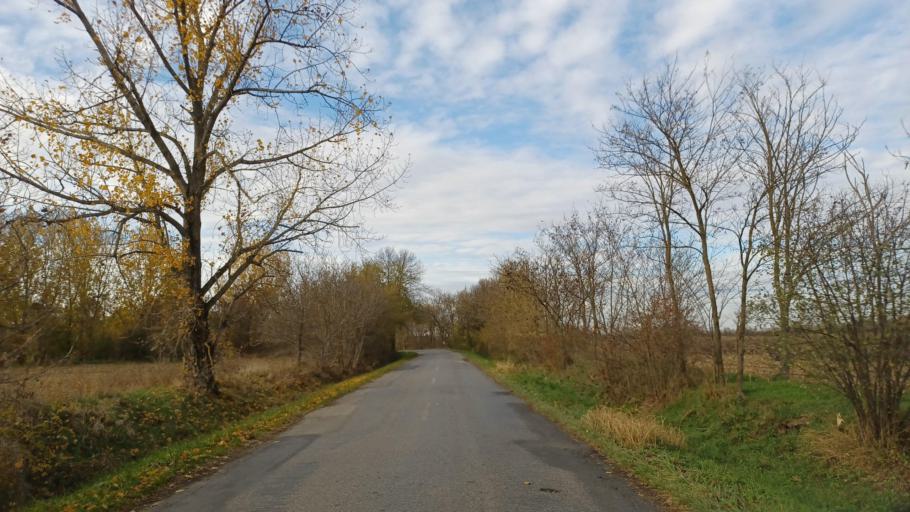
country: HU
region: Fejer
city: Cece
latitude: 46.7173
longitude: 18.6239
